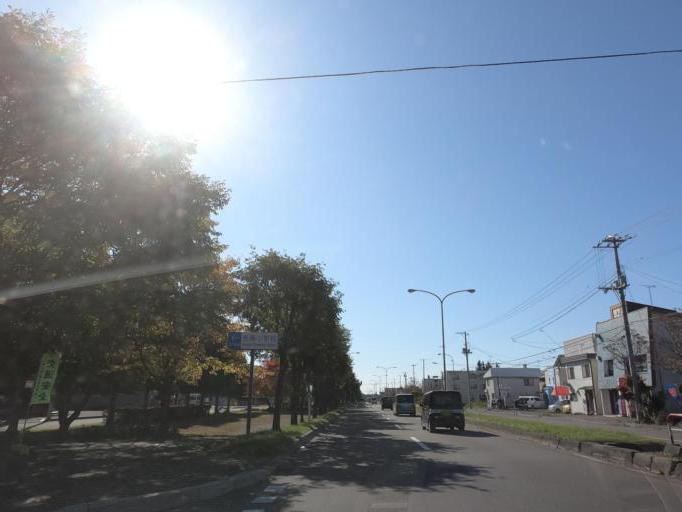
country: JP
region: Hokkaido
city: Obihiro
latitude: 42.9090
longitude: 143.2138
